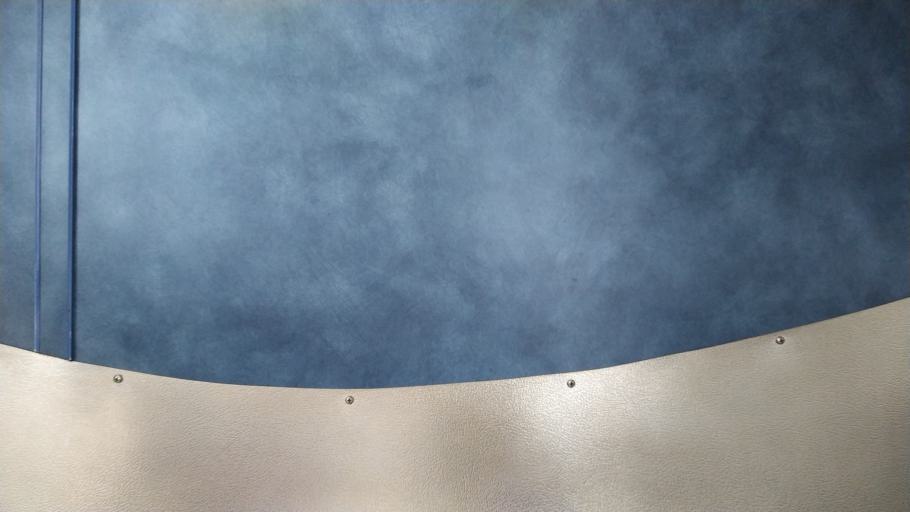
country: DE
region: Hamburg
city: Altona
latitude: 53.5464
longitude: 9.8629
